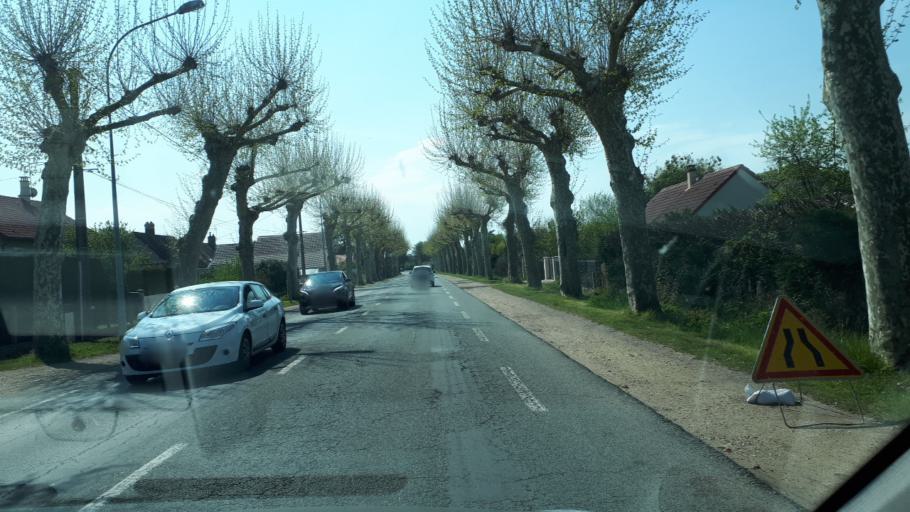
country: FR
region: Centre
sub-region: Departement du Loir-et-Cher
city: Romorantin-Lanthenay
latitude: 47.3752
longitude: 1.7367
